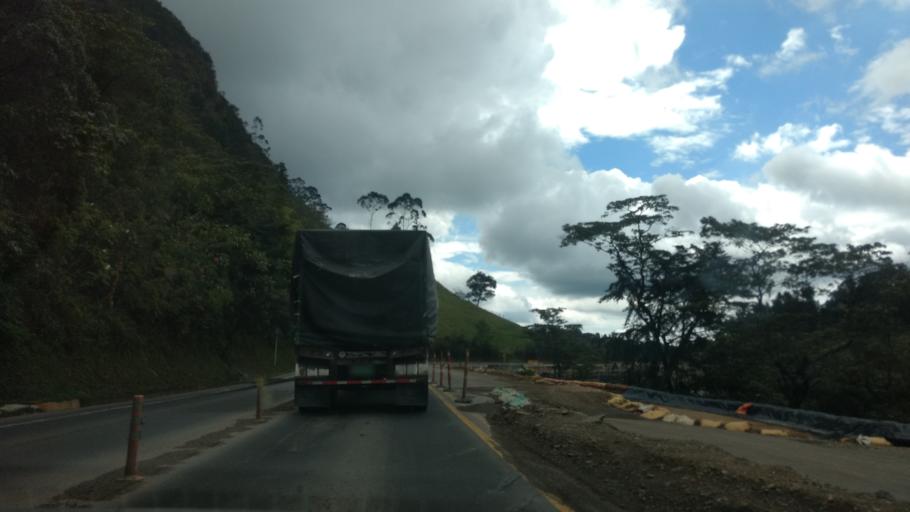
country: CO
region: Cundinamarca
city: San Francisco
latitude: 4.9293
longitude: -74.2953
